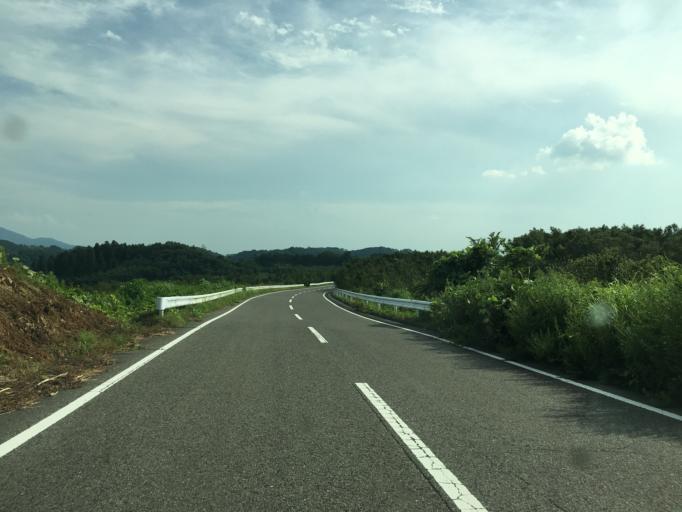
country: JP
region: Fukushima
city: Koriyama
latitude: 37.3828
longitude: 140.4445
